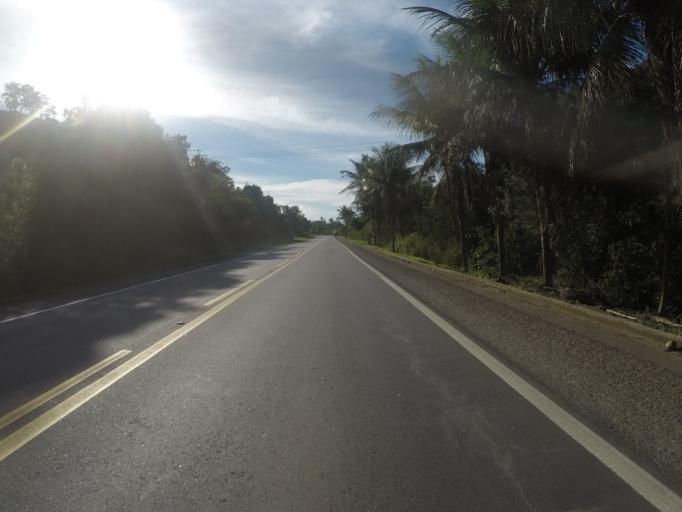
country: BR
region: Espirito Santo
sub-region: Fundao
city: Fundao
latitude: -19.9008
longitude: -40.4091
